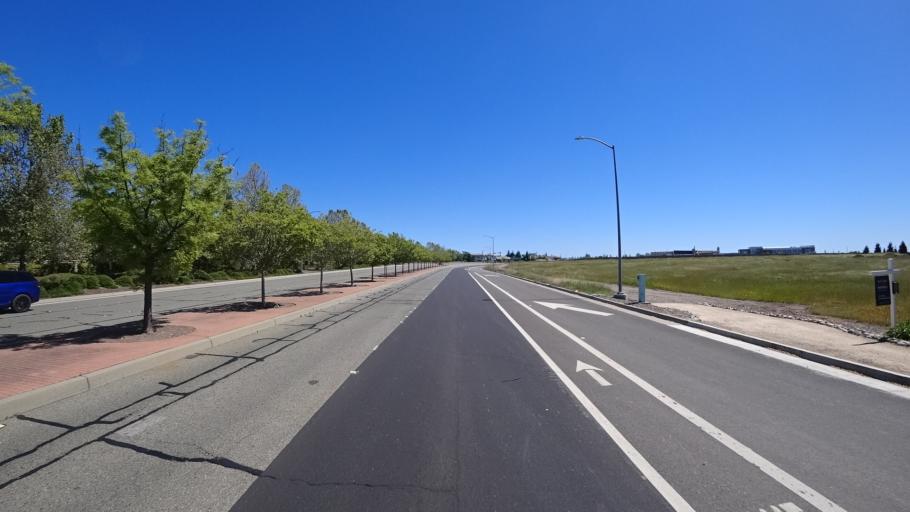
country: US
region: California
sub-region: Placer County
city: Rocklin
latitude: 38.7726
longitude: -121.2136
